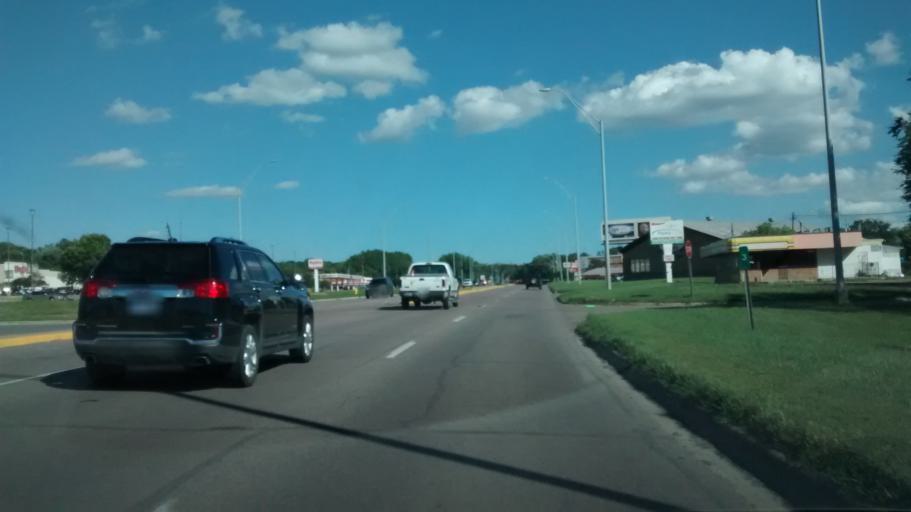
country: US
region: Iowa
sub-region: Woodbury County
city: Sioux City
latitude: 42.4889
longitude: -96.3667
